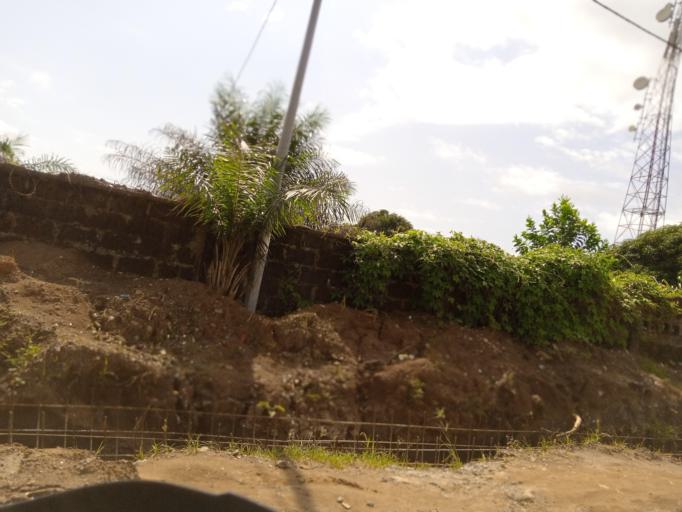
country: SL
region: Northern Province
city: Masoyila
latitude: 8.6130
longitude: -13.2046
